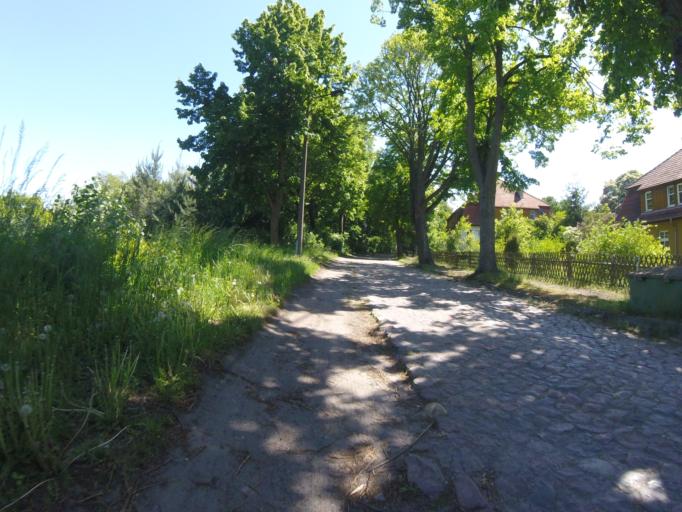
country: DE
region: Brandenburg
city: Teupitz
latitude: 52.1350
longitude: 13.6213
